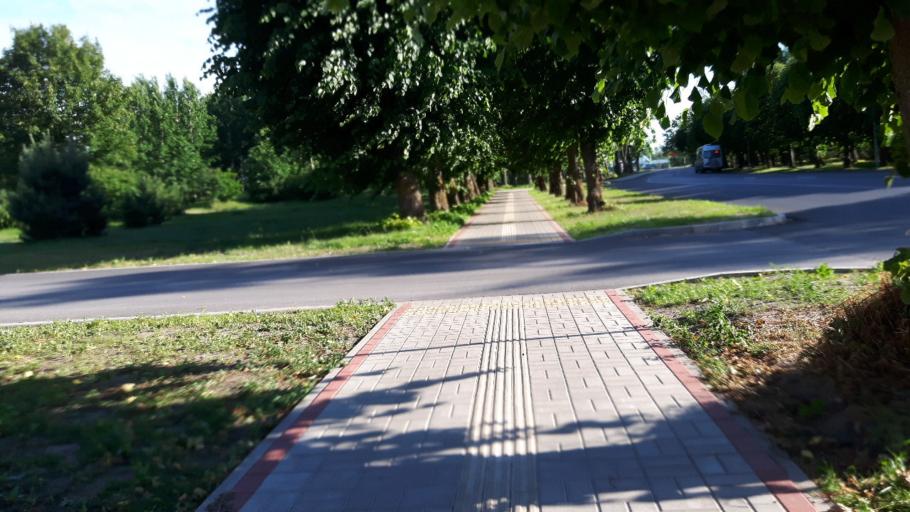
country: LV
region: Liepaja
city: Vec-Liepaja
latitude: 56.5475
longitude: 21.0060
